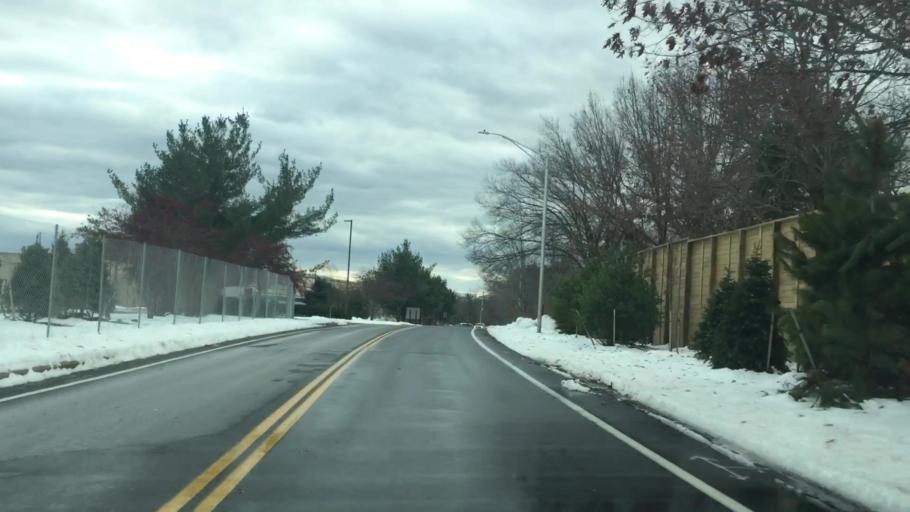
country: US
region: New Hampshire
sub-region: Rockingham County
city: Salem
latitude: 42.7719
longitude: -71.2329
